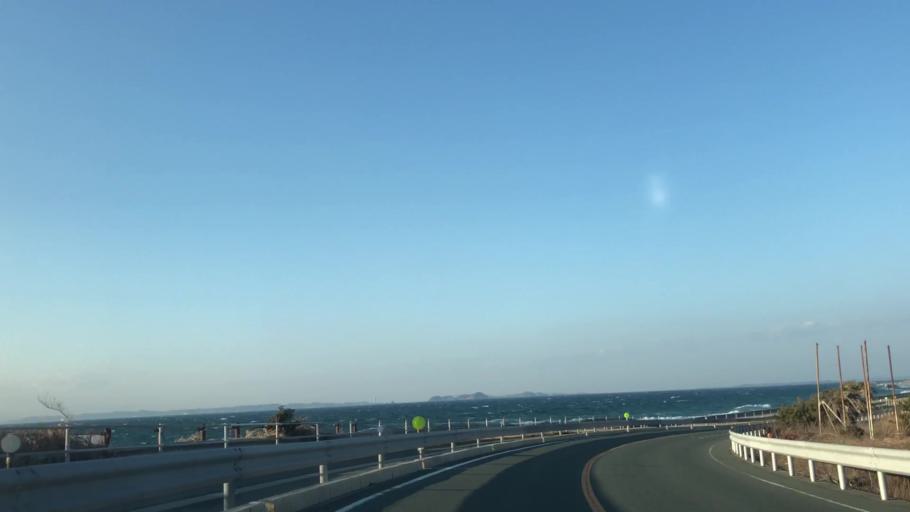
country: JP
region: Aichi
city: Toyohama
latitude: 34.5887
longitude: 137.0273
